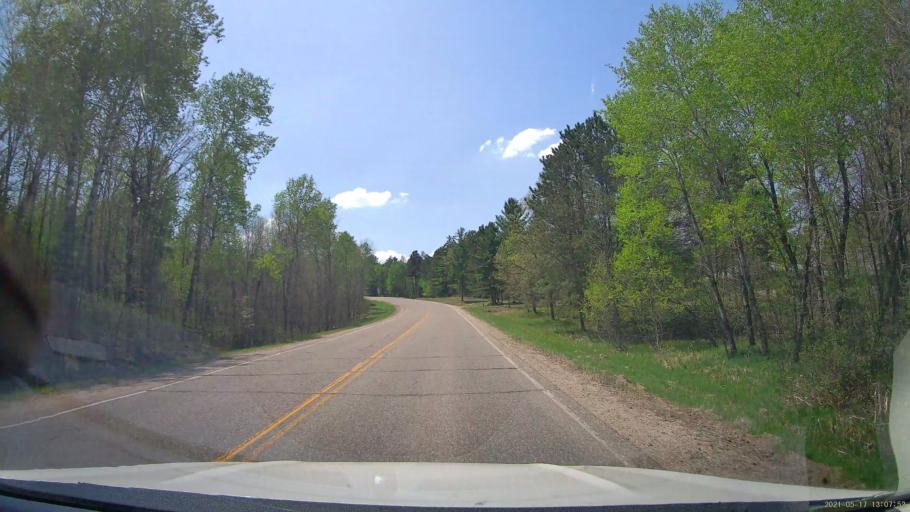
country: US
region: Minnesota
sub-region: Hubbard County
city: Park Rapids
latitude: 47.0446
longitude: -94.9165
